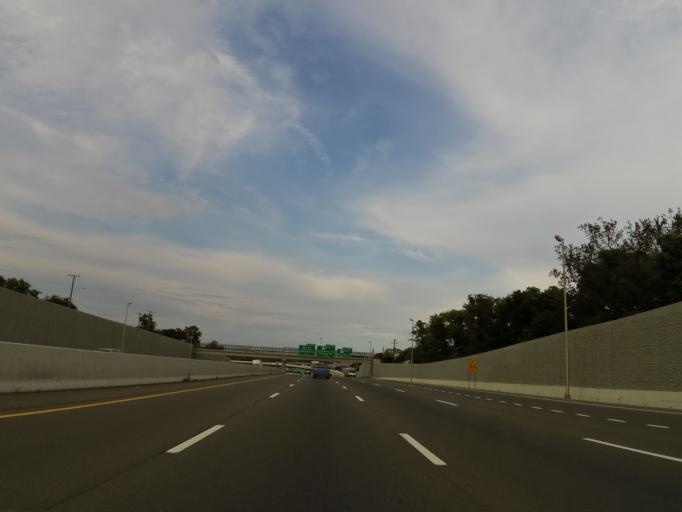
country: US
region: Tennessee
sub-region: Davidson County
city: Belle Meade
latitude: 36.1506
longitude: -86.8655
